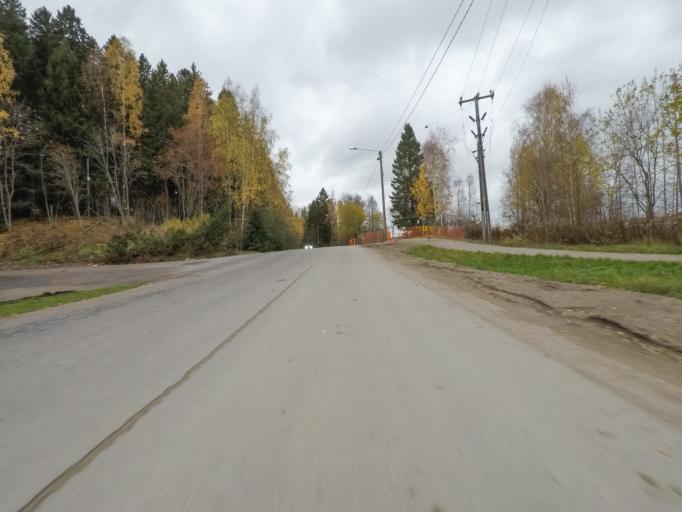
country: FI
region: Uusimaa
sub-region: Porvoo
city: Porvoo
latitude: 60.3824
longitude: 25.6678
